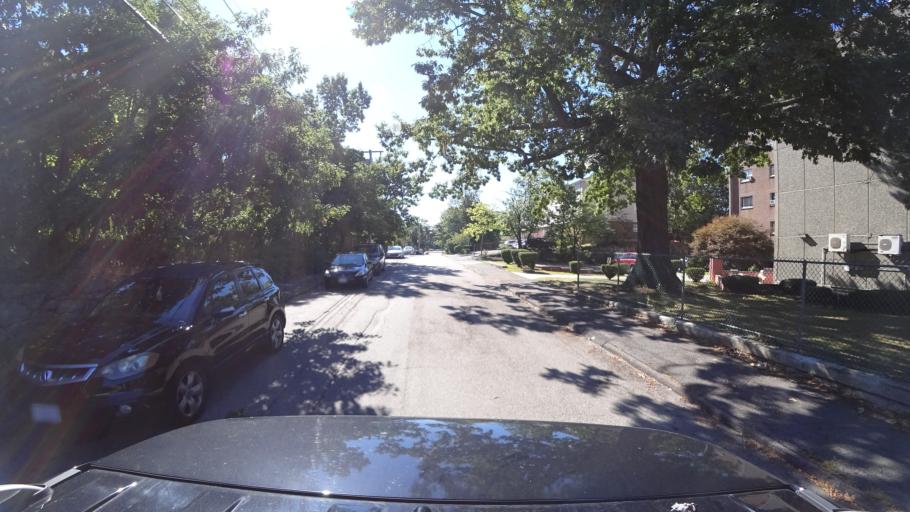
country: US
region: Massachusetts
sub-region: Norfolk County
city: Dedham
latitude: 42.2586
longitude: -71.1596
